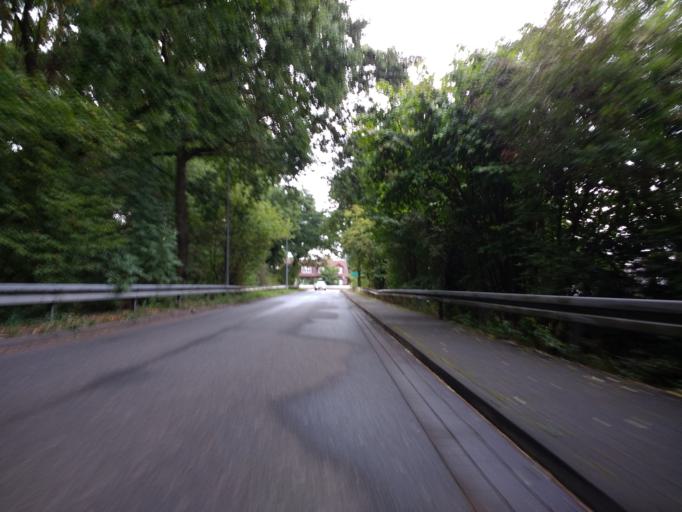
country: DE
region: Lower Saxony
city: Wolfsburg
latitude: 52.4276
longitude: 10.7493
